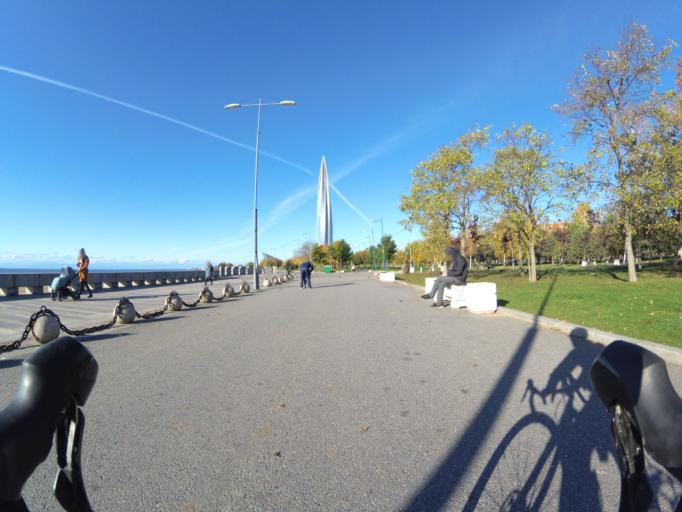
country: RU
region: Leningrad
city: Untolovo
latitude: 59.9820
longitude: 30.1971
